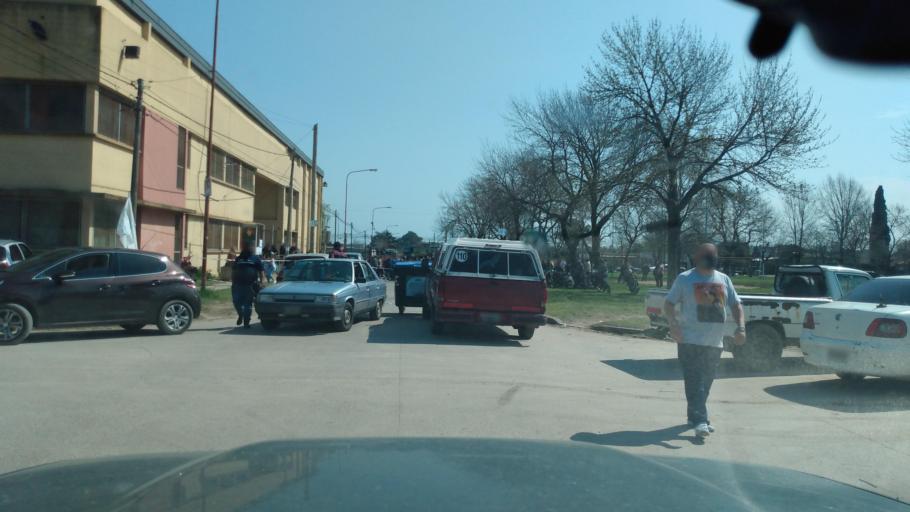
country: AR
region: Buenos Aires
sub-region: Partido de Lujan
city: Lujan
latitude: -34.5484
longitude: -59.1035
